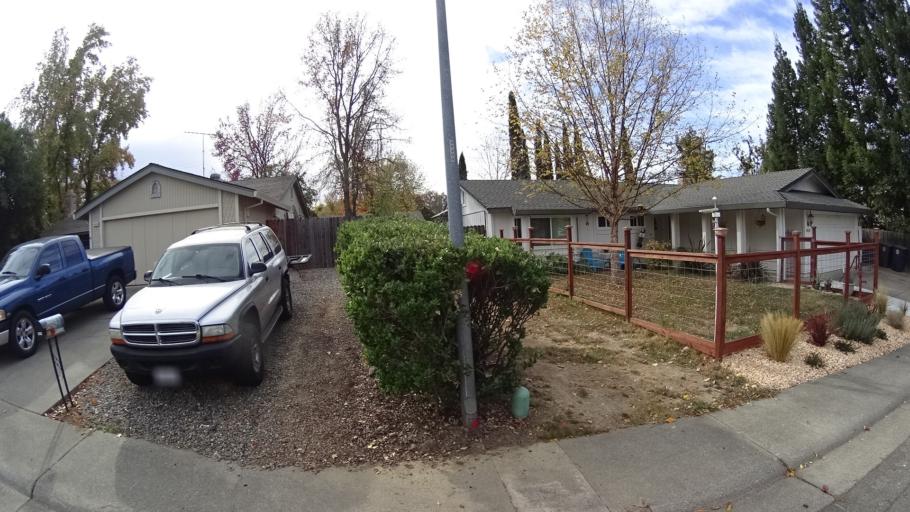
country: US
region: California
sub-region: Sacramento County
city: Citrus Heights
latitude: 38.7093
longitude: -121.2465
